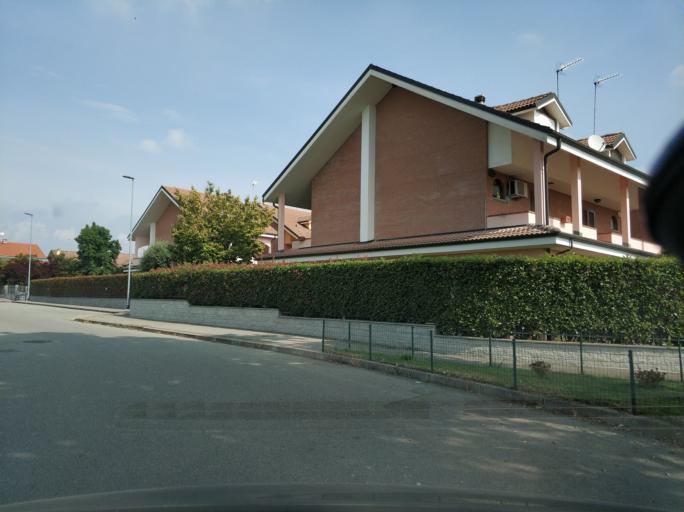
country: IT
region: Piedmont
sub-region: Provincia di Torino
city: San Maurizio
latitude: 45.1988
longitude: 7.6165
